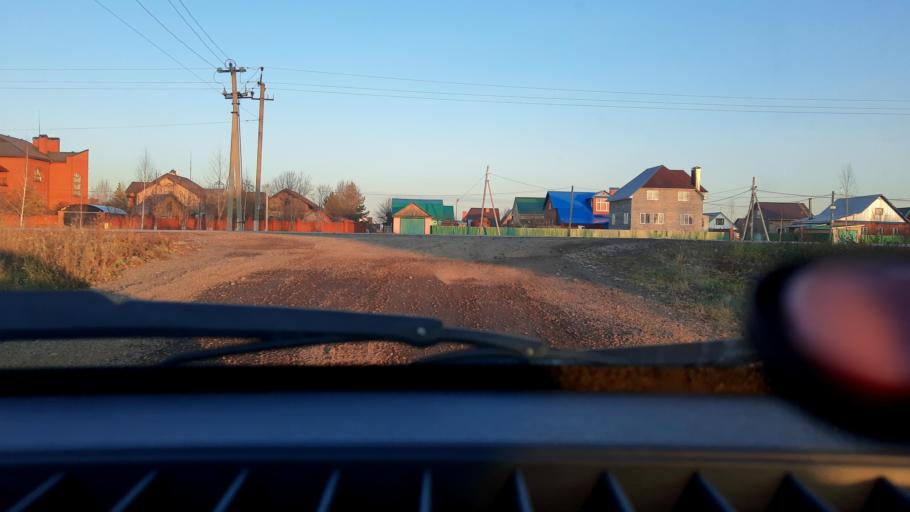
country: RU
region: Bashkortostan
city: Mikhaylovka
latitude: 54.8213
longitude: 55.8824
